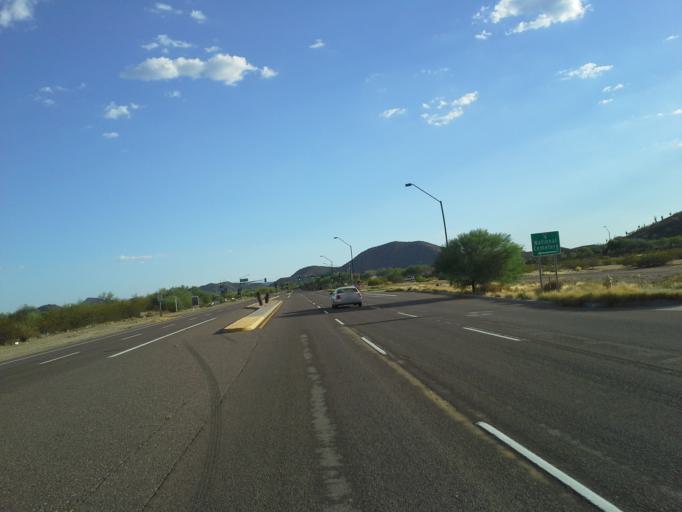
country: US
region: Arizona
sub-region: Maricopa County
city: Cave Creek
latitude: 33.7012
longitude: -112.0245
